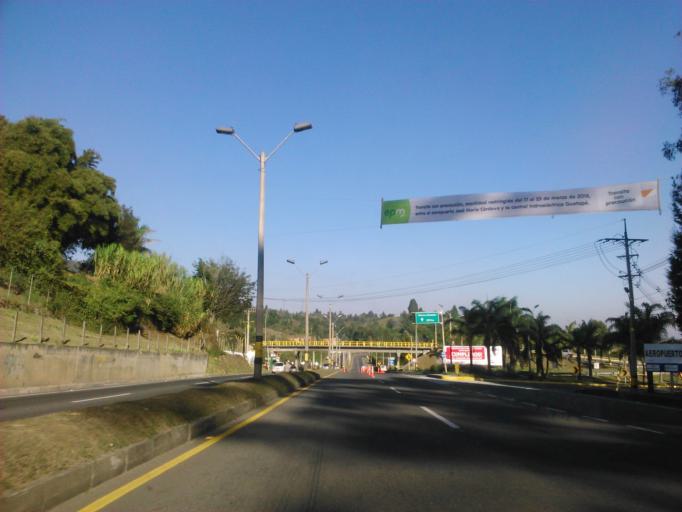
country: CO
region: Antioquia
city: Guarne
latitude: 6.2533
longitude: -75.4311
